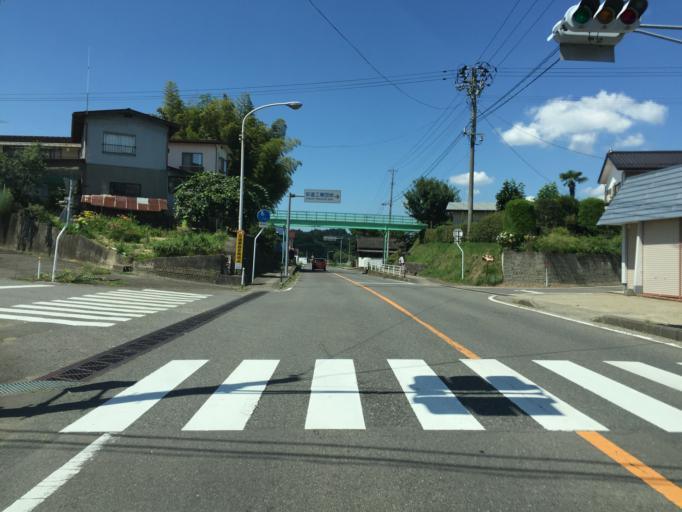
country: JP
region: Fukushima
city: Nihommatsu
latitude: 37.6234
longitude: 140.4620
